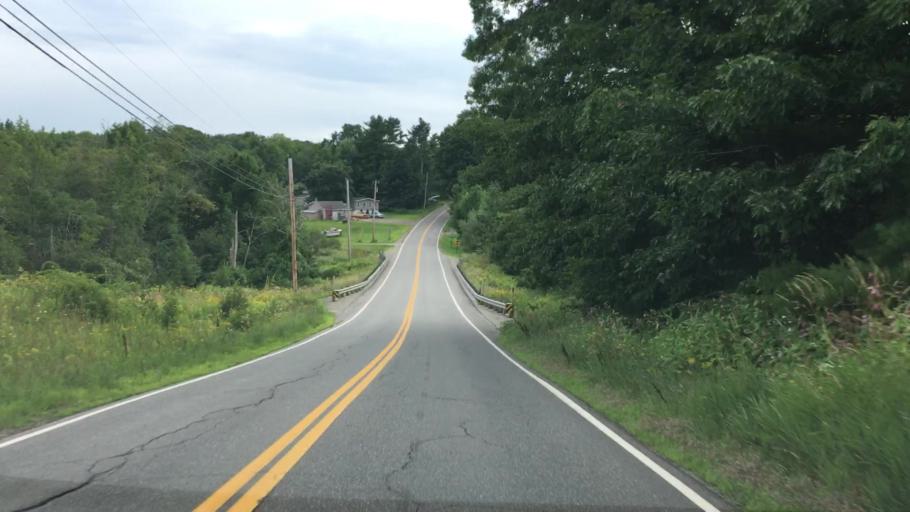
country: US
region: Maine
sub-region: Knox County
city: Hope
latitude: 44.3013
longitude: -69.1061
